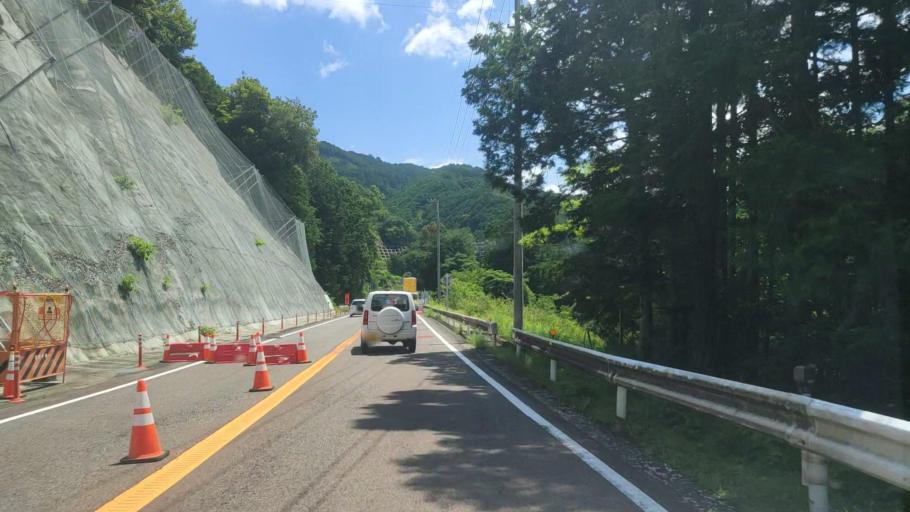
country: JP
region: Mie
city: Owase
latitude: 34.1017
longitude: 136.1992
